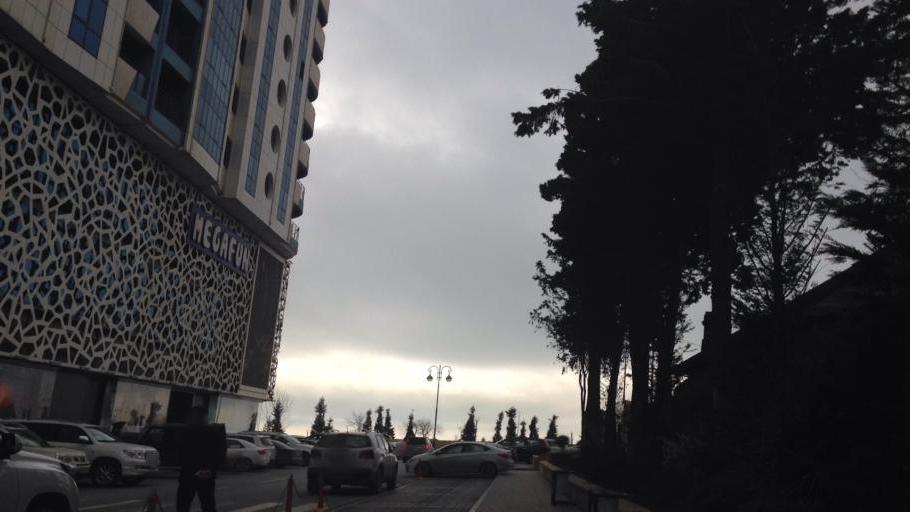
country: AZ
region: Baki
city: Baku
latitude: 40.3783
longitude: 49.8736
